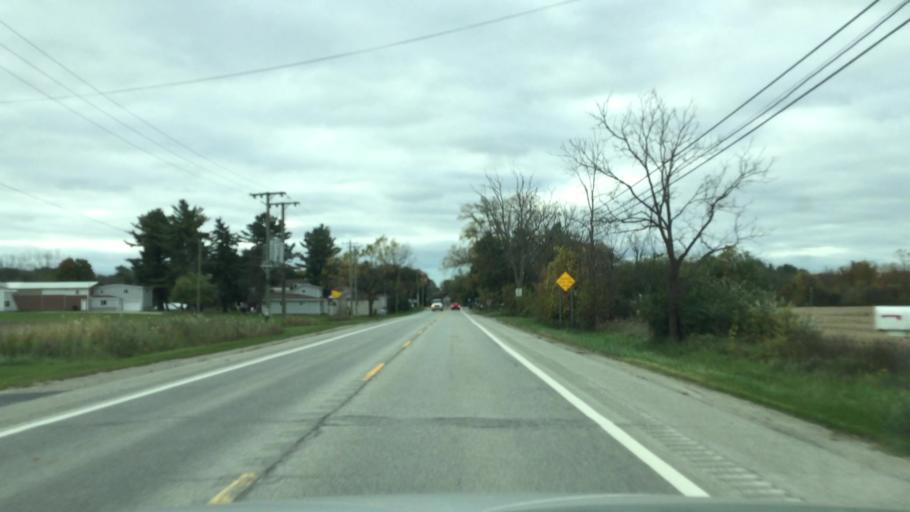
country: US
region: Michigan
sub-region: Macomb County
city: Memphis
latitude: 42.9058
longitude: -82.7697
